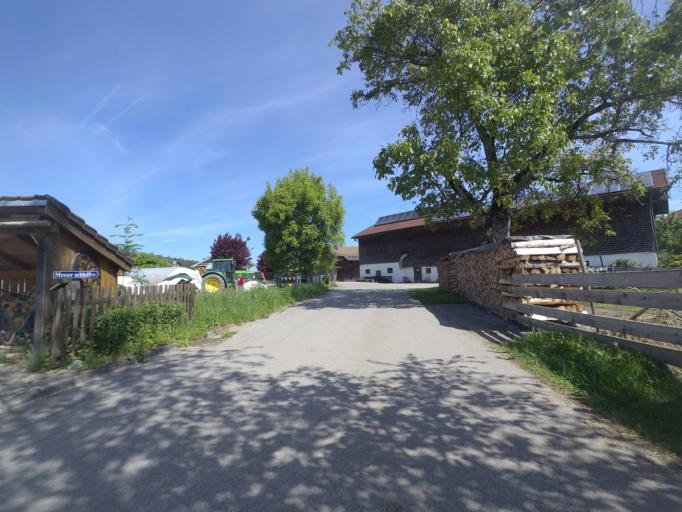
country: DE
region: Bavaria
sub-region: Upper Bavaria
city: Petting
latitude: 47.8948
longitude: 12.8196
